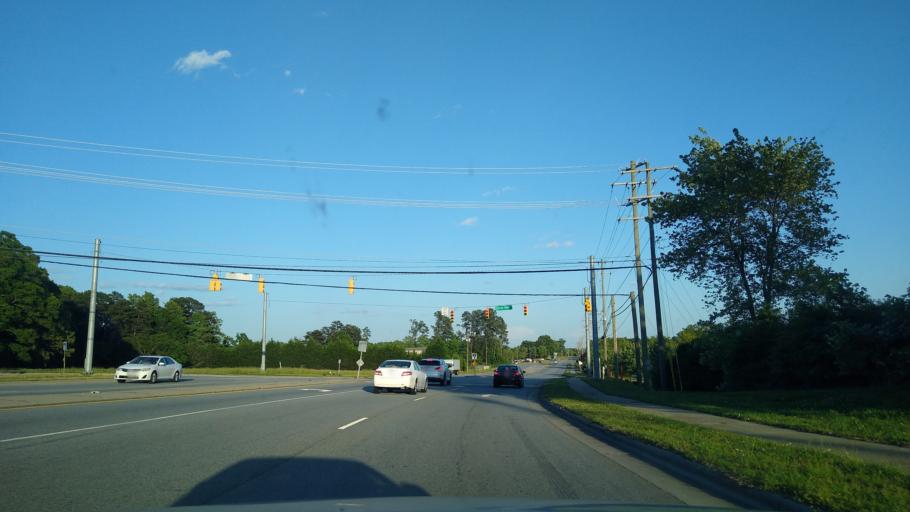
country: US
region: North Carolina
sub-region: Guilford County
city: Oak Ridge
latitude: 36.1041
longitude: -79.9847
